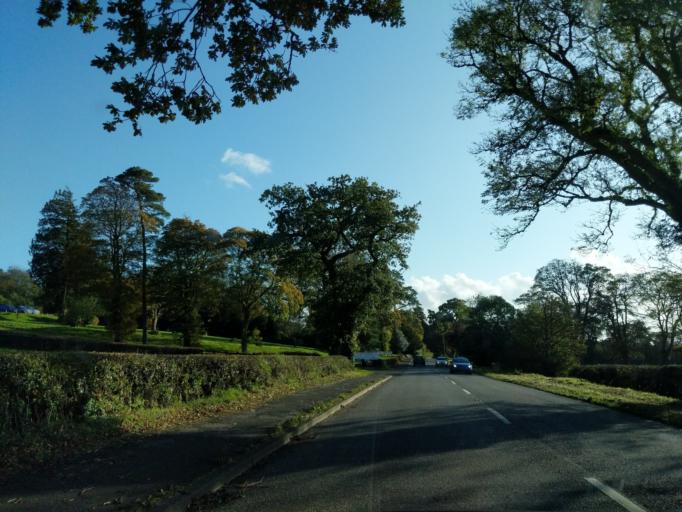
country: GB
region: Scotland
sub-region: Dumfries and Galloway
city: Kirkcudbright
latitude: 54.8530
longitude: -4.0402
